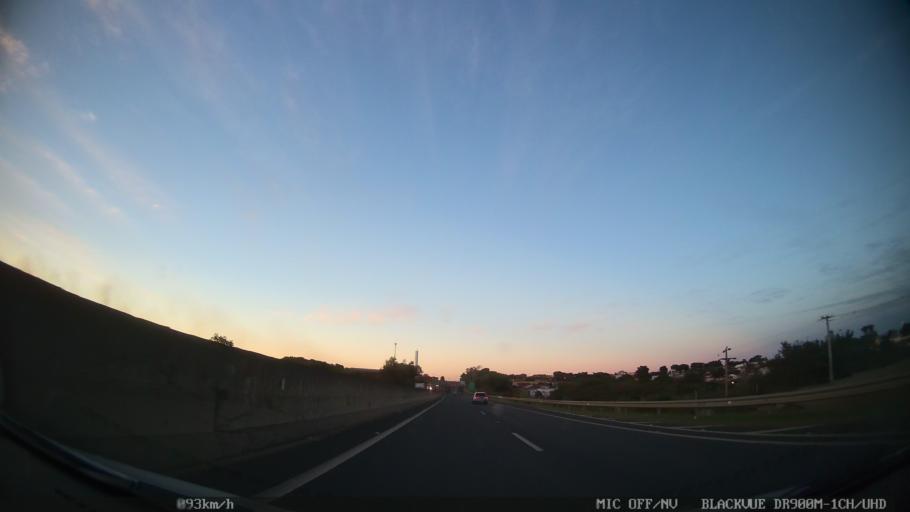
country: BR
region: Sao Paulo
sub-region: Catanduva
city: Catanduva
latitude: -21.1137
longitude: -48.9737
